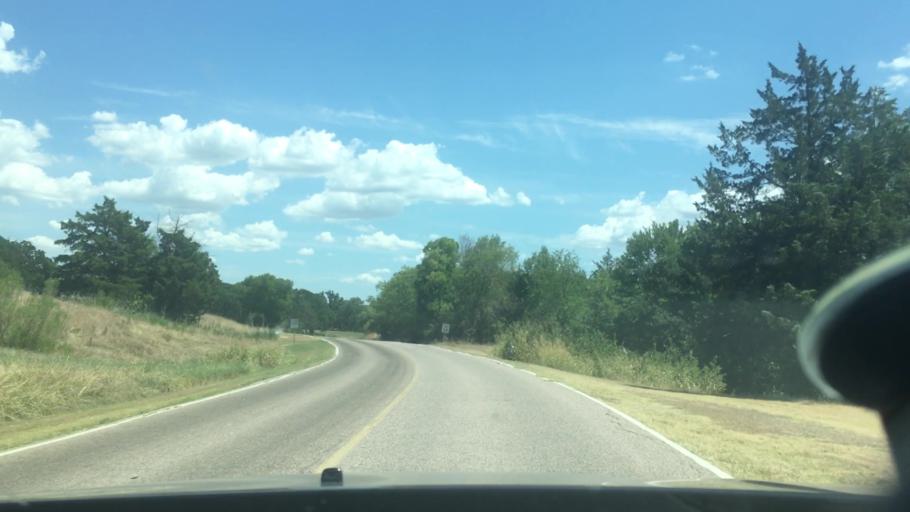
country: US
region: Oklahoma
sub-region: Marshall County
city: Kingston
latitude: 33.9921
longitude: -96.6409
